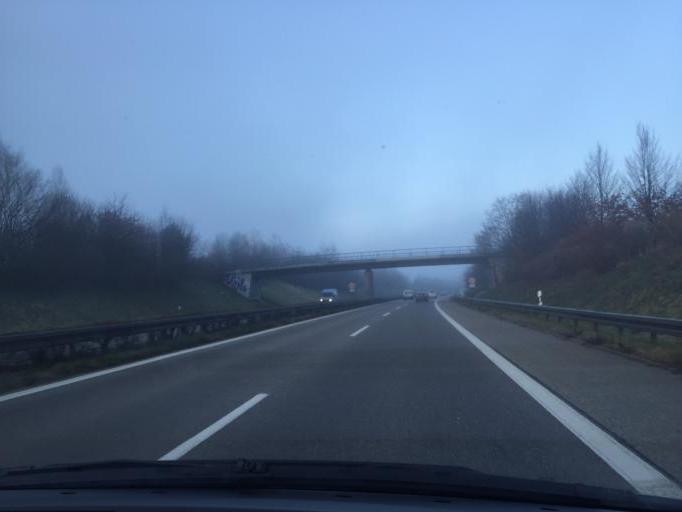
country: DE
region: Baden-Wuerttemberg
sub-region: Freiburg Region
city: Kirchzarten
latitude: 47.9739
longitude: 7.9263
